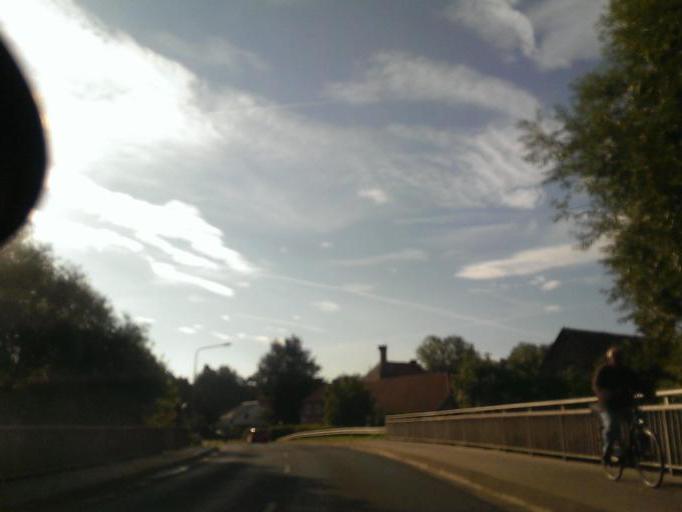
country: DE
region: Lower Saxony
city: Wunstorf
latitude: 52.4369
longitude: 9.4483
